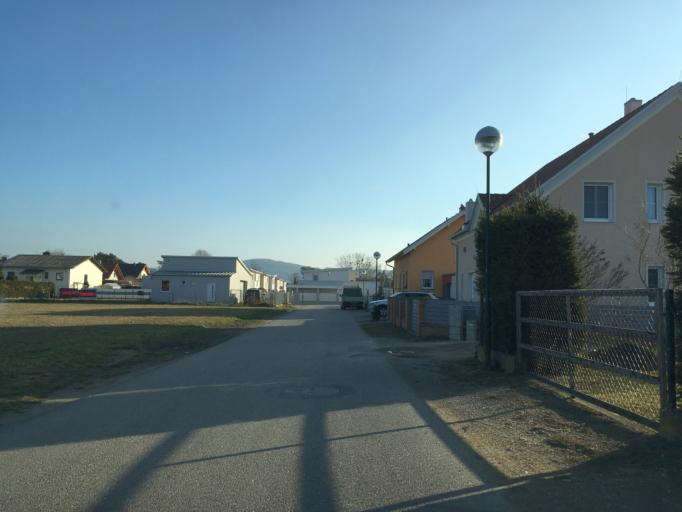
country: AT
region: Lower Austria
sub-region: Politischer Bezirk Tulln
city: Tulbing
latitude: 48.3294
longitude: 16.1187
